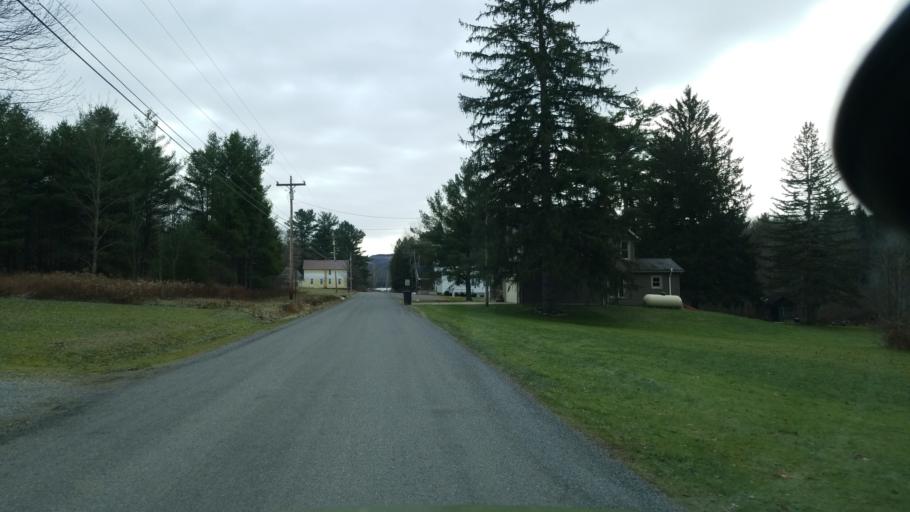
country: US
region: Pennsylvania
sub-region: Clearfield County
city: Treasure Lake
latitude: 41.1099
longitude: -78.6467
